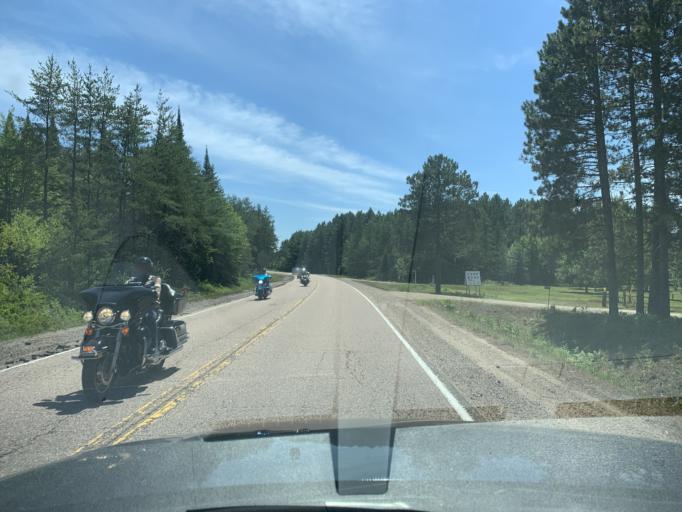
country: CA
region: Ontario
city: Petawawa
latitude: 45.6546
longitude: -77.5803
